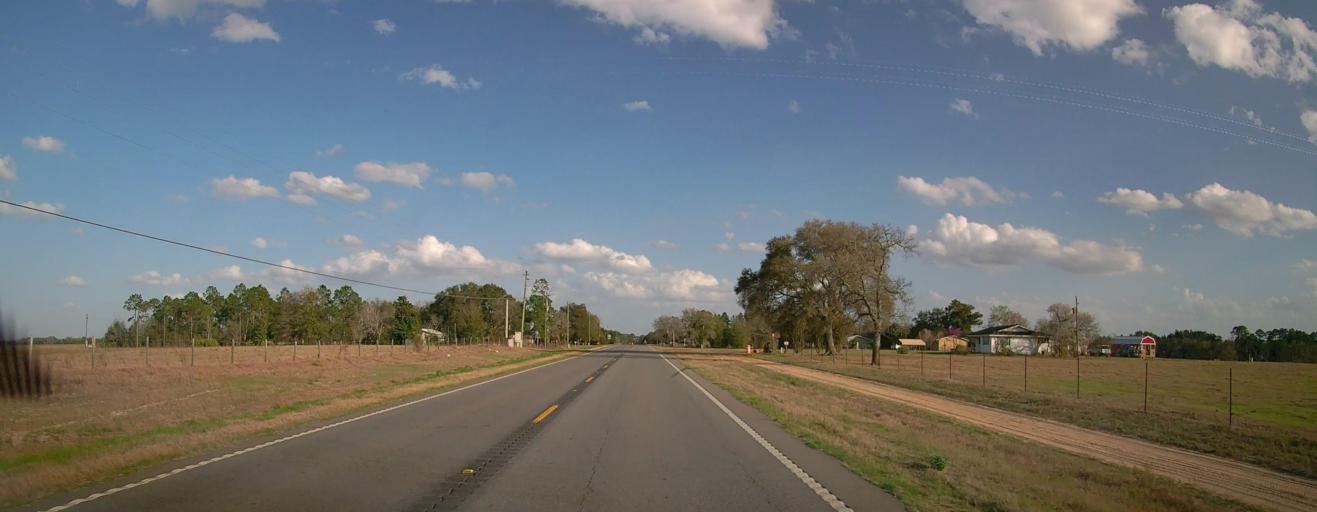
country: US
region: Georgia
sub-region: Tattnall County
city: Reidsville
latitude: 32.1002
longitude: -82.1624
